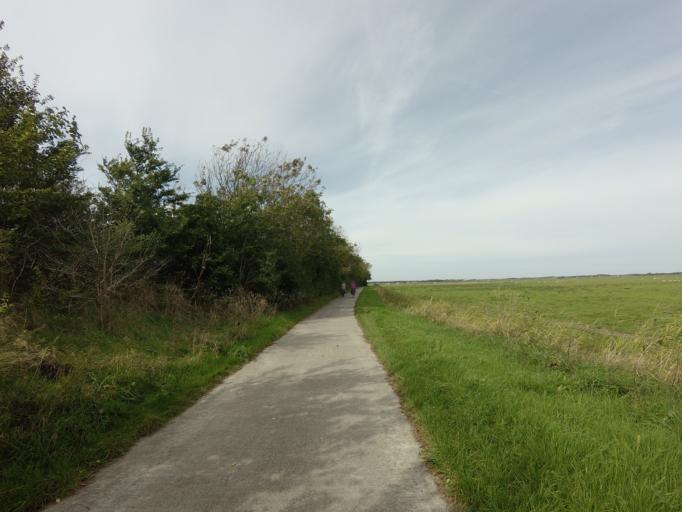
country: NL
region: North Holland
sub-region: Gemeente Texel
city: Den Burg
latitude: 53.0732
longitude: 4.8088
